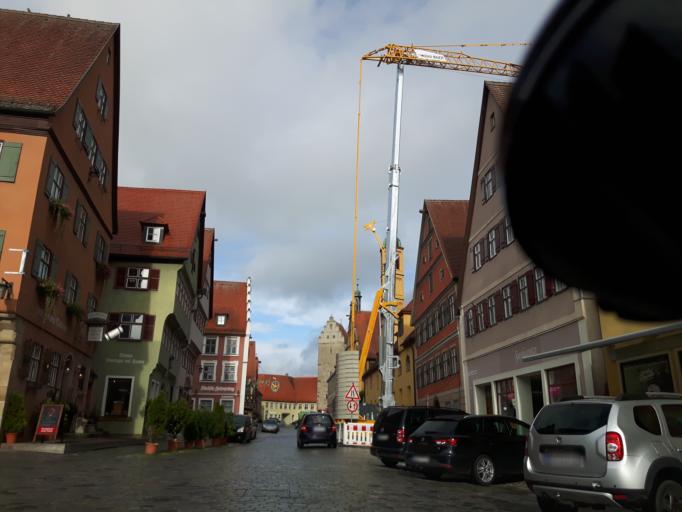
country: DE
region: Bavaria
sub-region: Regierungsbezirk Mittelfranken
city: Dinkelsbuhl
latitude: 49.0702
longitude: 10.3188
